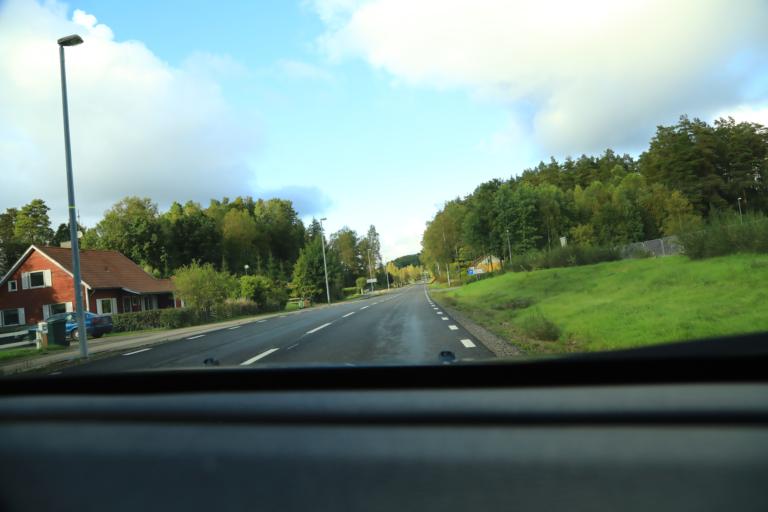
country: SE
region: Halland
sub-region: Halmstads Kommun
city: Getinge
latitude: 57.1292
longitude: 12.7156
